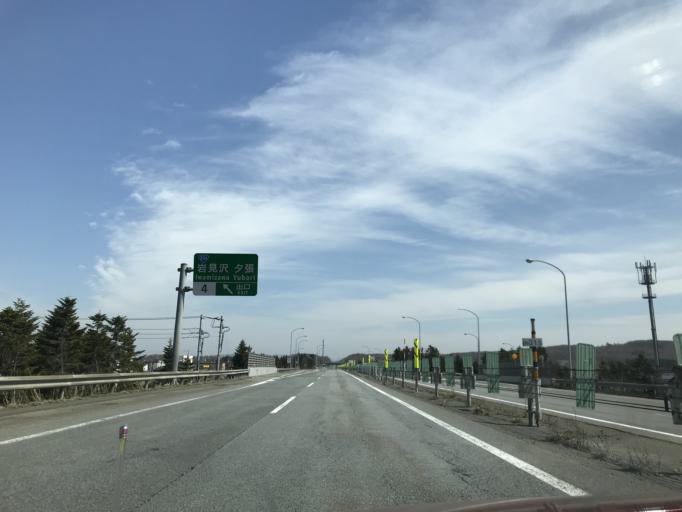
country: JP
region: Hokkaido
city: Iwamizawa
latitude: 43.1722
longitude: 141.7621
